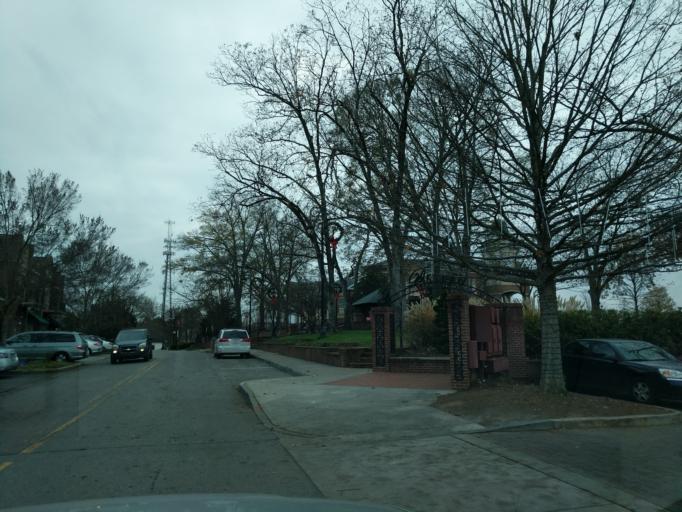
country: US
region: Georgia
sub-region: Gwinnett County
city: Duluth
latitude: 34.0023
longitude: -84.1457
